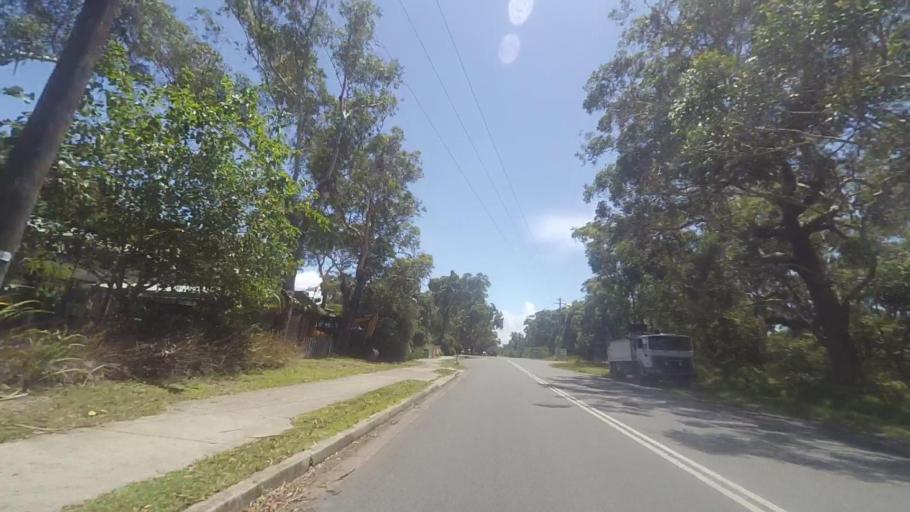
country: AU
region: New South Wales
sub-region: Great Lakes
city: Hawks Nest
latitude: -32.6692
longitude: 152.1780
